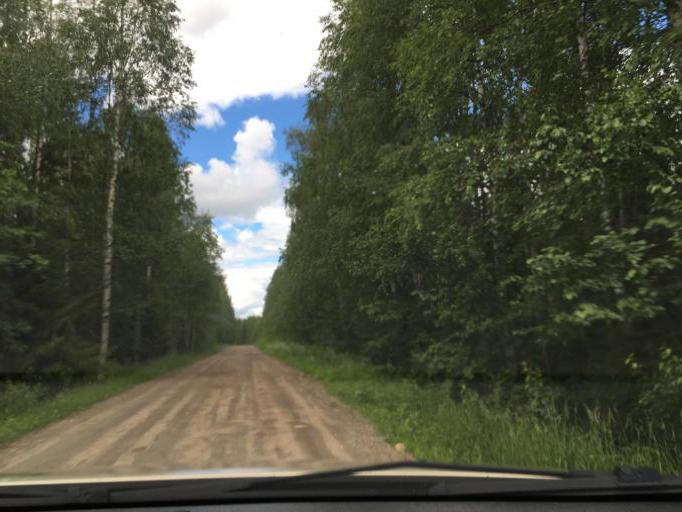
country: SE
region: Norrbotten
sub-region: Overkalix Kommun
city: OEverkalix
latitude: 66.1244
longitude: 22.7852
